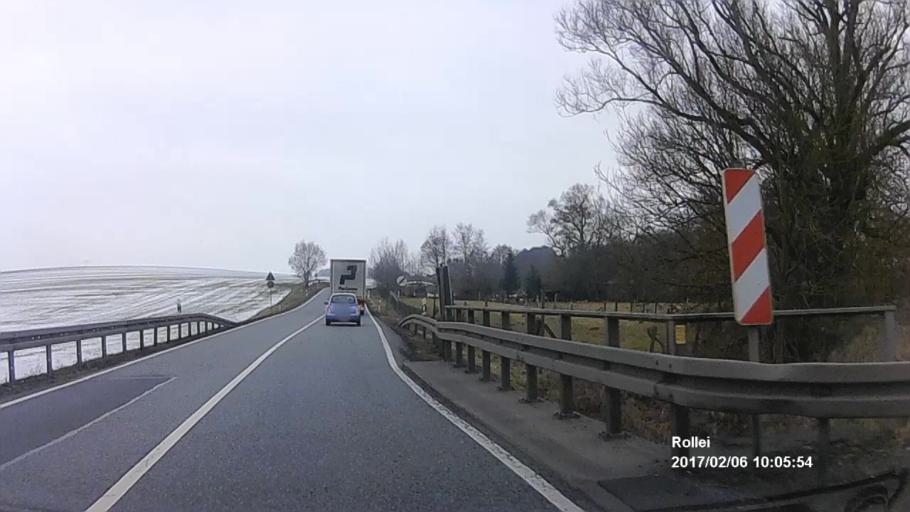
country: DE
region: Thuringia
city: Etzelsrode
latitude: 51.5331
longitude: 10.6117
